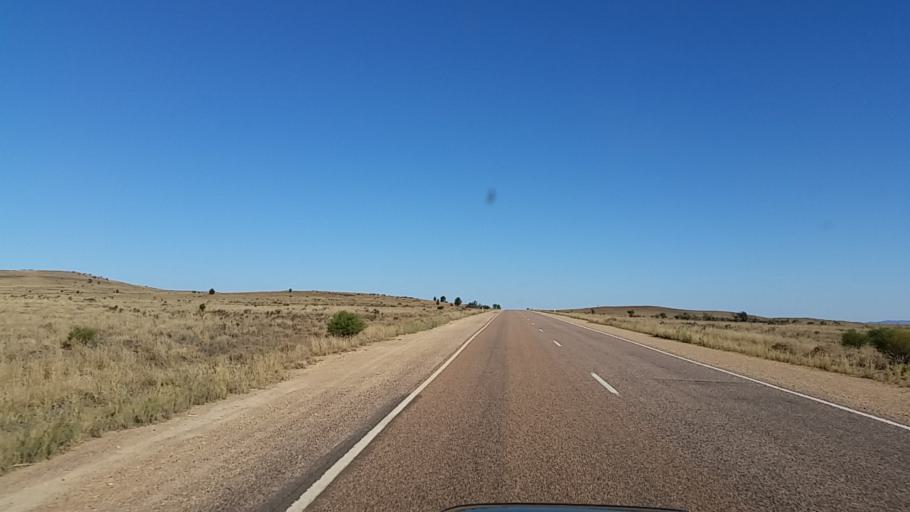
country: AU
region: South Australia
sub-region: Peterborough
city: Peterborough
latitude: -32.5587
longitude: 138.5631
